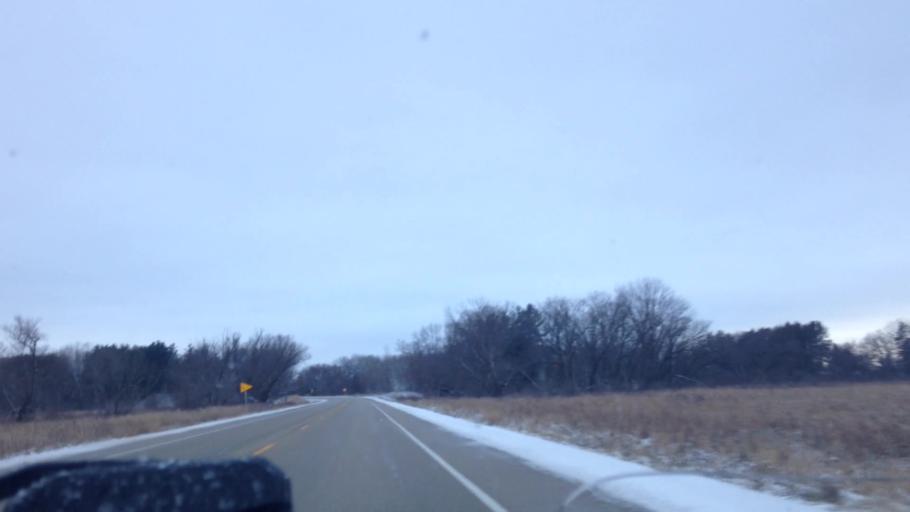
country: US
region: Wisconsin
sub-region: Dodge County
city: Horicon
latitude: 43.4629
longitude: -88.6154
